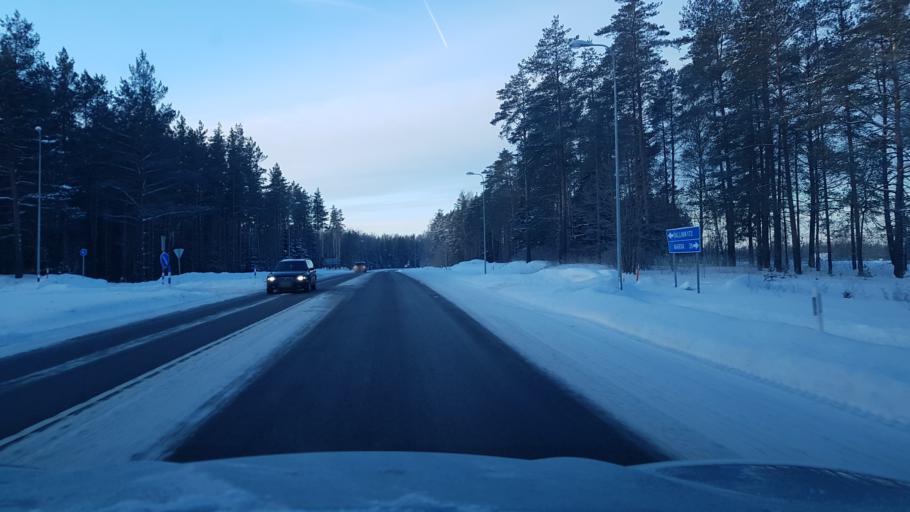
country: EE
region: Ida-Virumaa
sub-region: Toila vald
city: Voka
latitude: 59.3841
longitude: 27.5682
